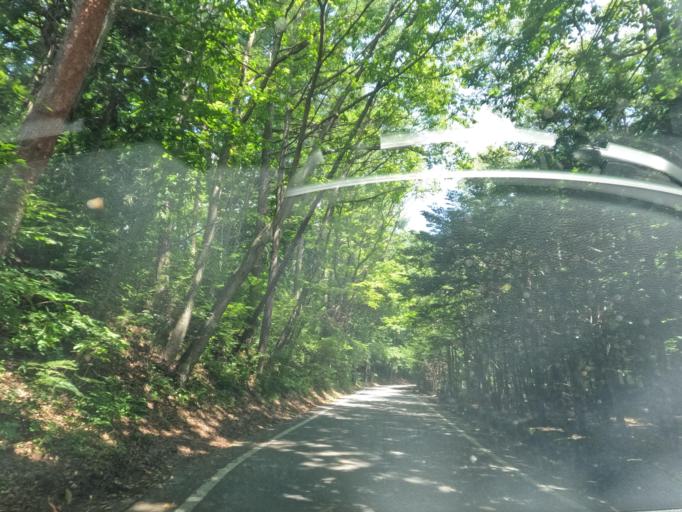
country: JP
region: Nagano
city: Komoro
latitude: 36.3595
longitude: 138.5967
